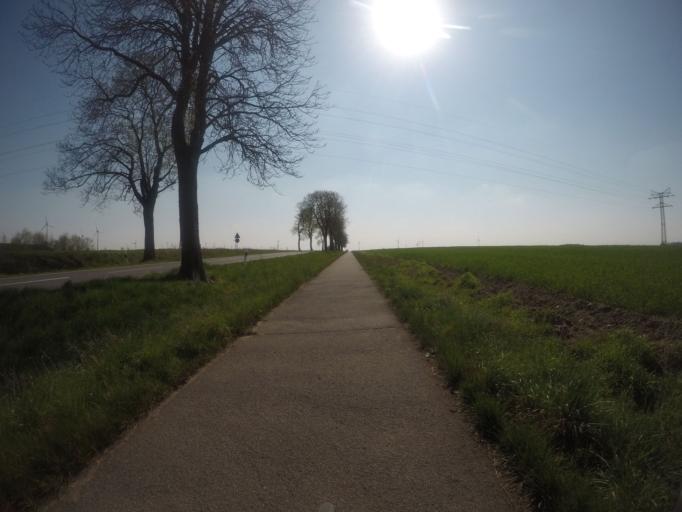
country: DE
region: Brandenburg
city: Nauen
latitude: 52.5686
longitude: 12.8697
